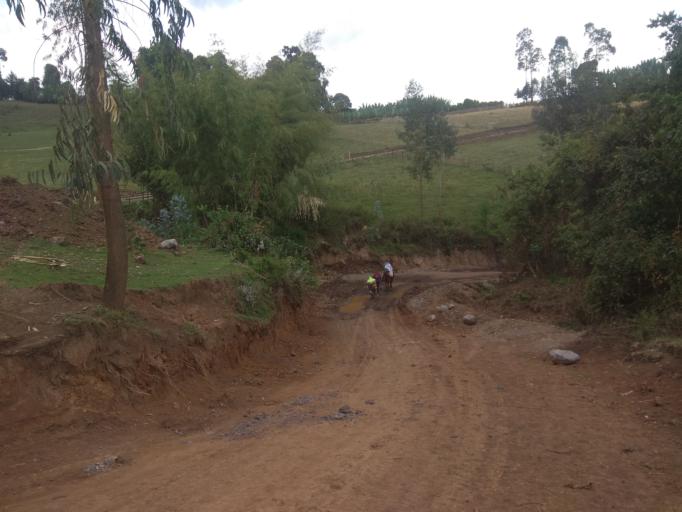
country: ET
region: Oromiya
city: Guder
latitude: 8.7486
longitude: 37.6303
